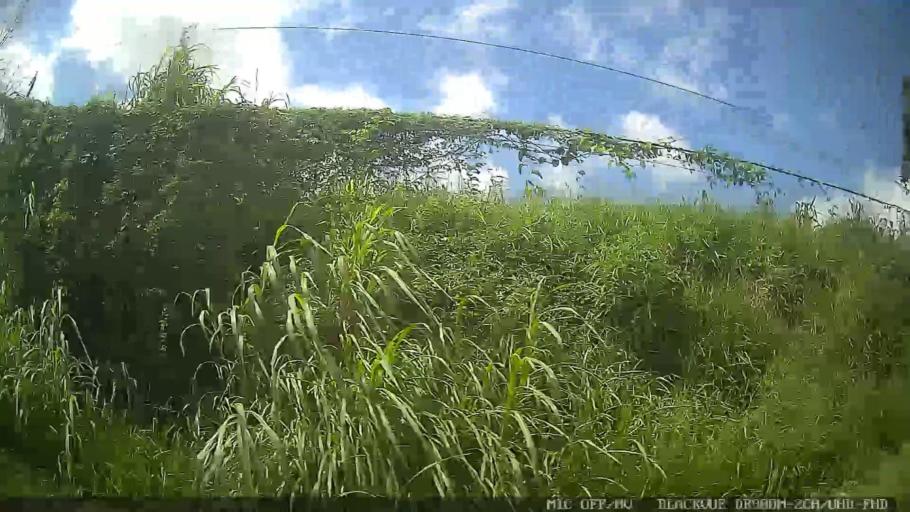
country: BR
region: Sao Paulo
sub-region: Amparo
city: Amparo
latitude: -22.8619
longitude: -46.7580
